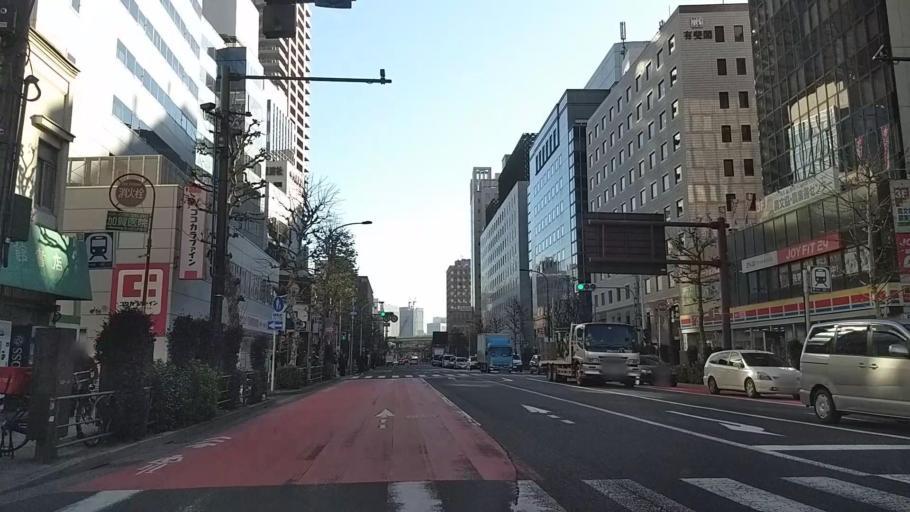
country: JP
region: Tokyo
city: Tokyo
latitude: 35.6958
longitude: 139.7582
